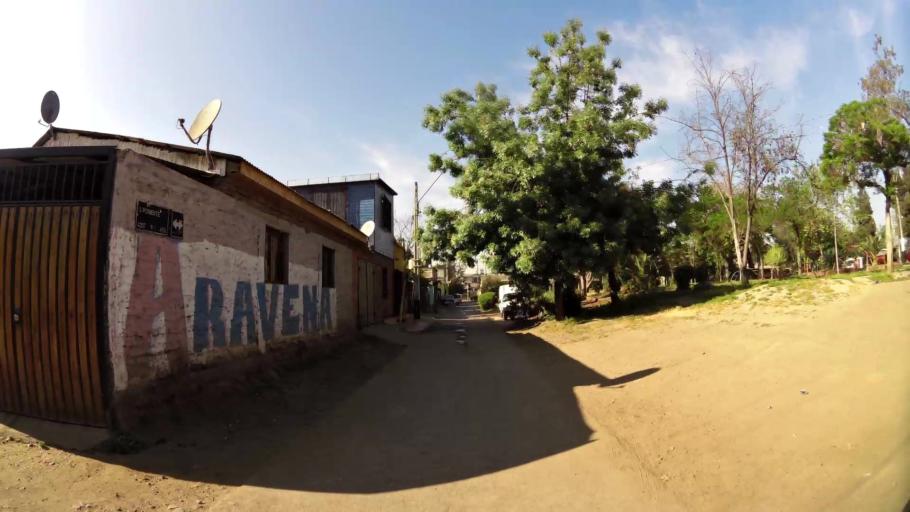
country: CL
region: Santiago Metropolitan
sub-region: Provincia de Santiago
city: Lo Prado
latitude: -33.3915
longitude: -70.6846
